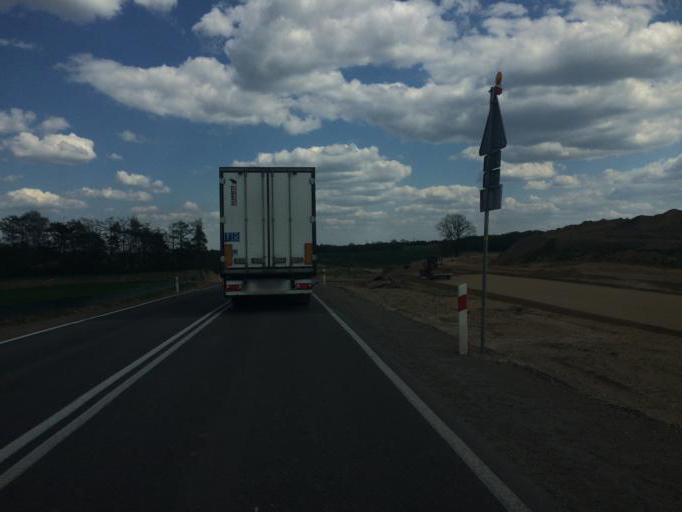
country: PL
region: Warmian-Masurian Voivodeship
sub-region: Powiat ostrodzki
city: Ostroda
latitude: 53.6867
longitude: 20.0060
